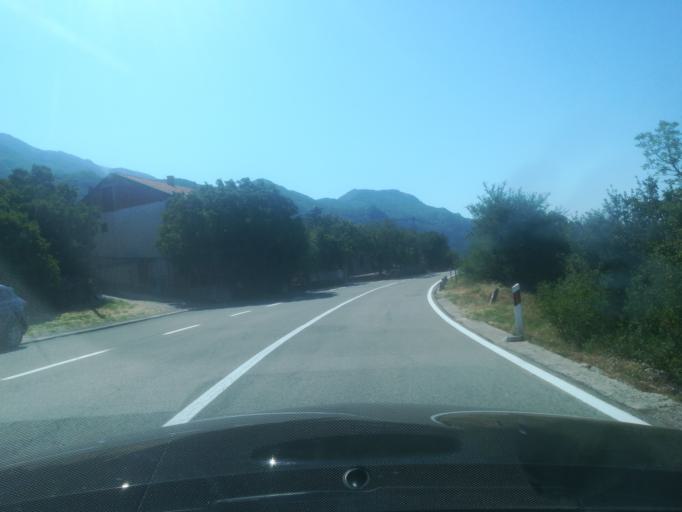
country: HR
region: Primorsko-Goranska
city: Banjol
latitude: 44.7490
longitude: 14.9048
